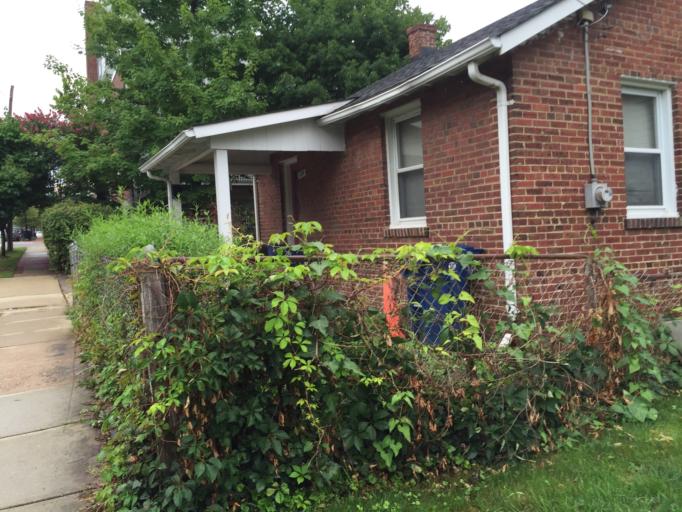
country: US
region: Virginia
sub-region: City of Alexandria
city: Alexandria
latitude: 38.8127
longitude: -77.0527
